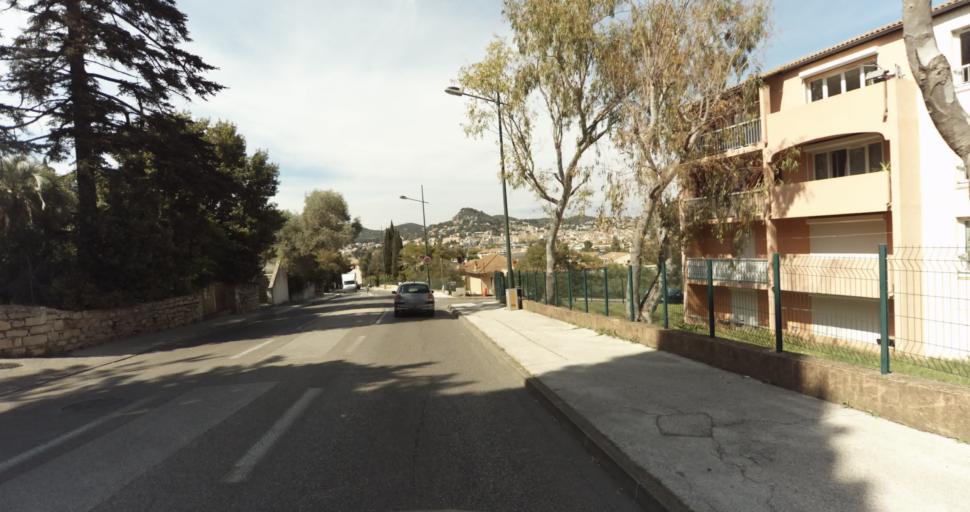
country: FR
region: Provence-Alpes-Cote d'Azur
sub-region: Departement du Var
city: Hyeres
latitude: 43.1055
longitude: 6.1217
